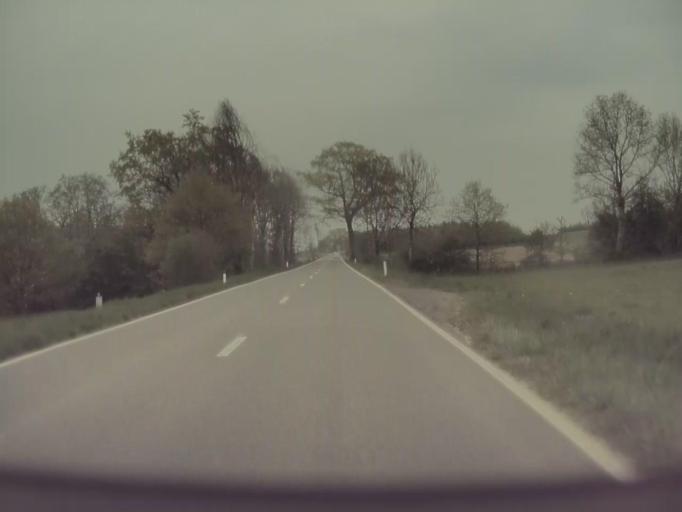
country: BE
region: Wallonia
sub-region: Province de Liege
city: Ferrieres
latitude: 50.4149
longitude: 5.5782
